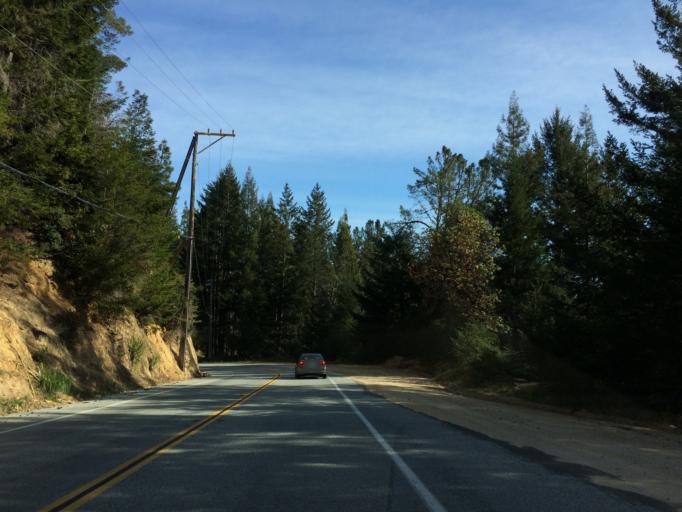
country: US
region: California
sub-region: Santa Cruz County
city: Felton
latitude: 37.0296
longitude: -122.1053
